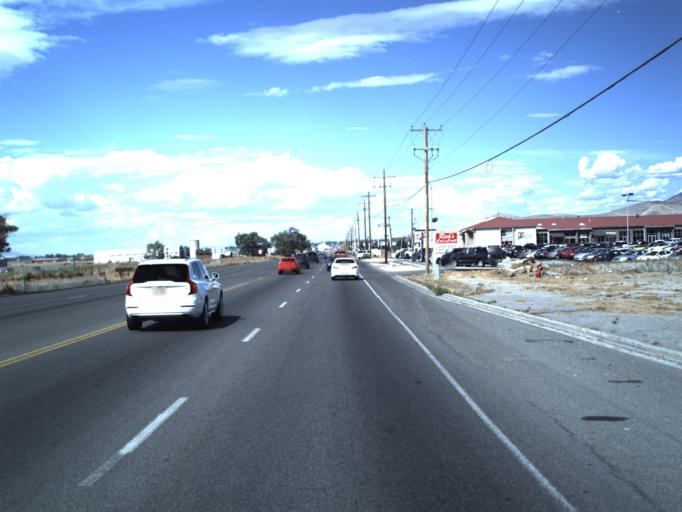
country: US
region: Utah
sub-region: Cache County
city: Hyde Park
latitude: 41.7782
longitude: -111.8339
